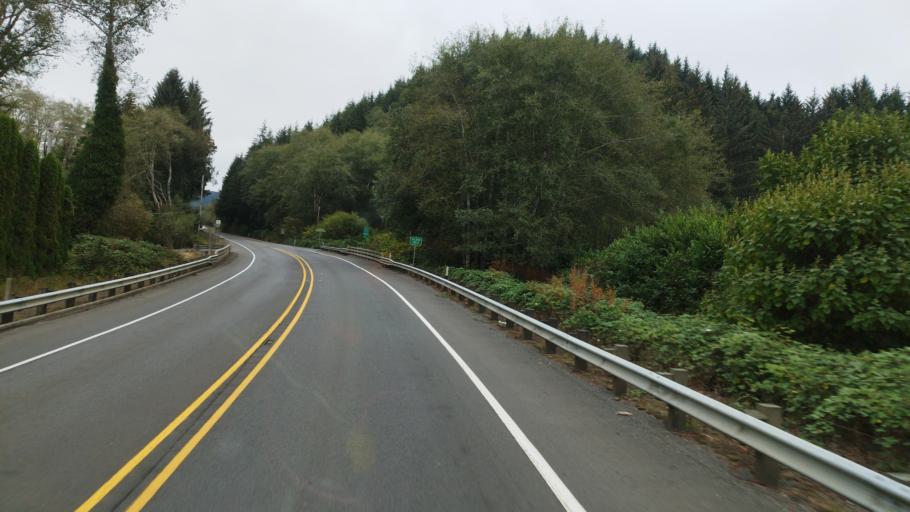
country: US
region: Oregon
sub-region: Clatsop County
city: Cannon Beach
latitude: 45.9193
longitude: -123.8948
